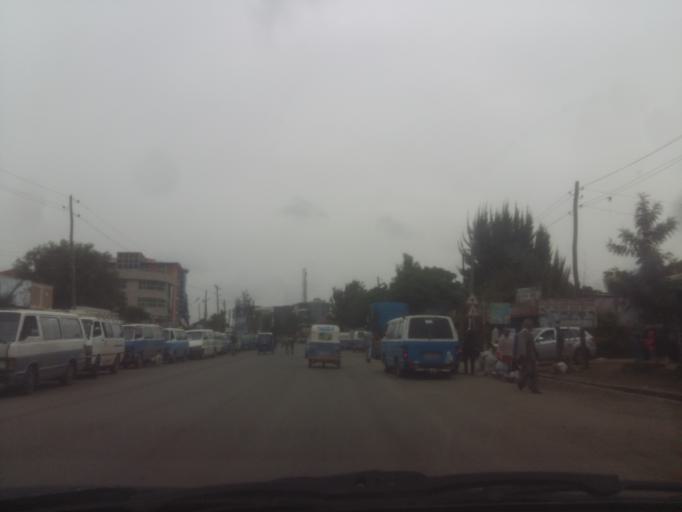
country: ET
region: Oromiya
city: Bishoftu
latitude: 8.7918
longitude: 38.9051
